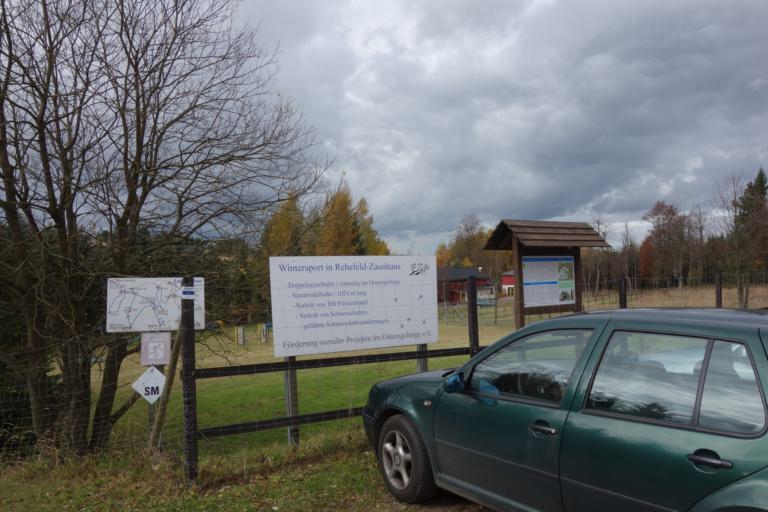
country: CZ
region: Ustecky
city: Hrob
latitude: 50.7204
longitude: 13.6878
